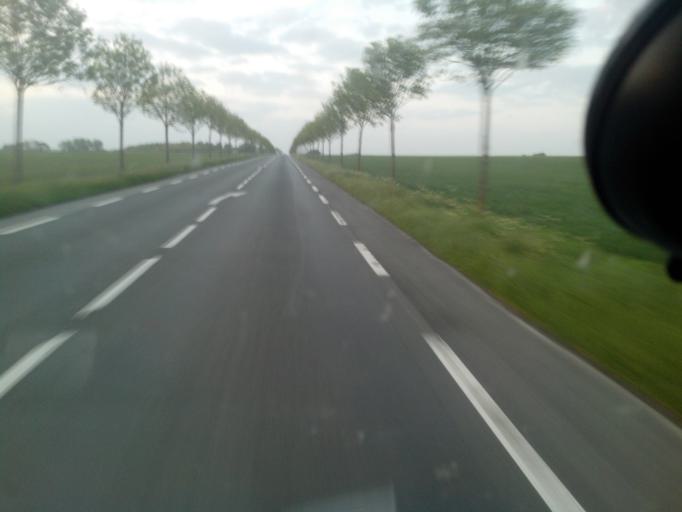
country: FR
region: Nord-Pas-de-Calais
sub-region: Departement du Pas-de-Calais
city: Hesdin
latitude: 50.3431
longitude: 2.0310
